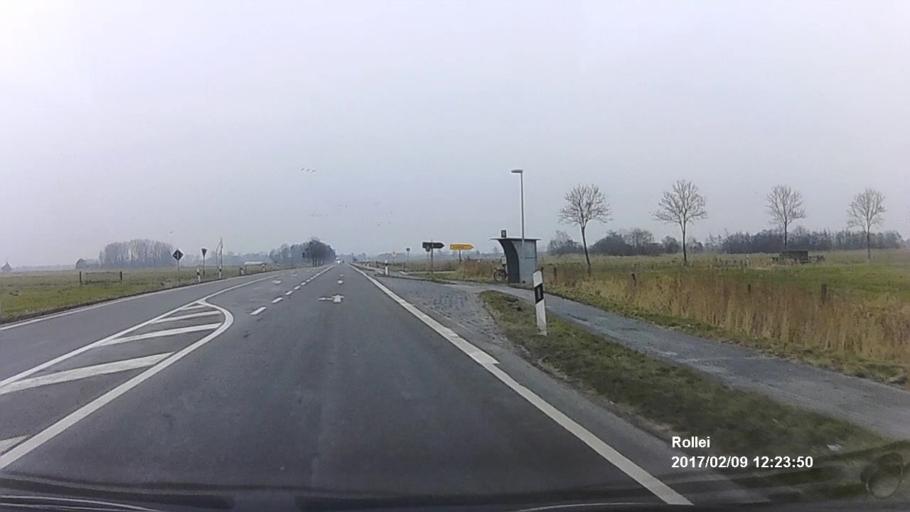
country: DE
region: Lower Saxony
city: Weener
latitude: 53.1875
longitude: 7.3838
